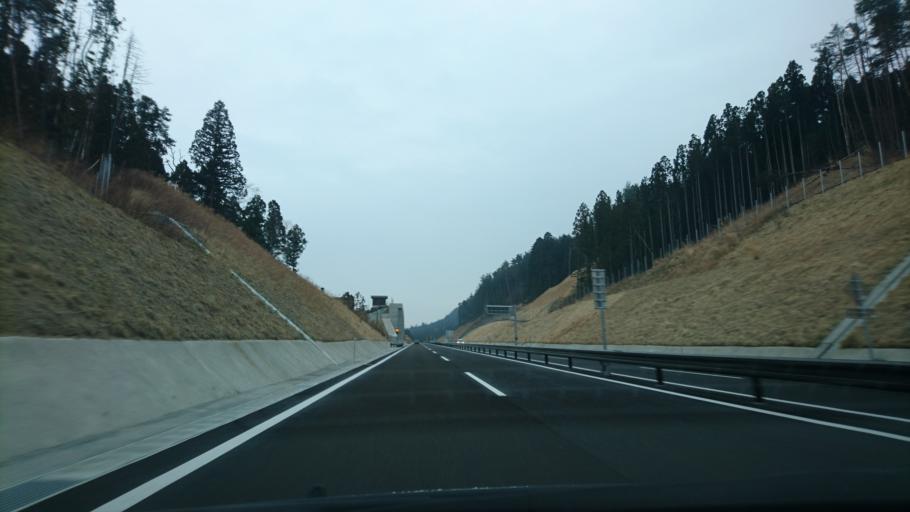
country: JP
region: Iwate
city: Ofunato
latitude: 38.9815
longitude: 141.6166
